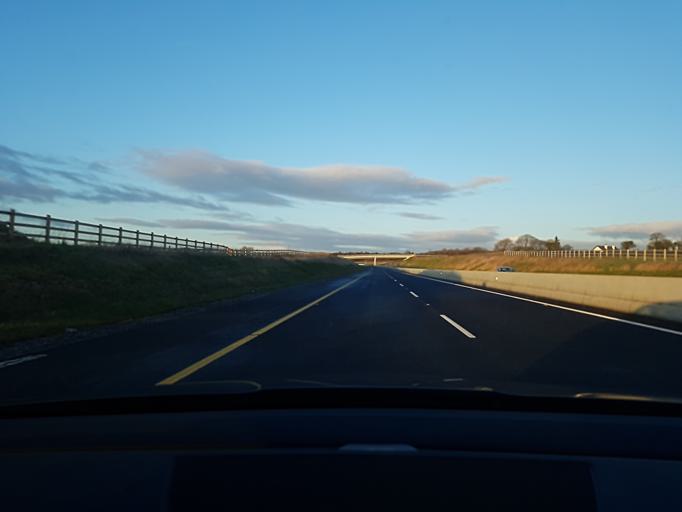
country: IE
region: Connaught
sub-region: County Galway
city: Athenry
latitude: 53.3577
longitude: -8.7919
